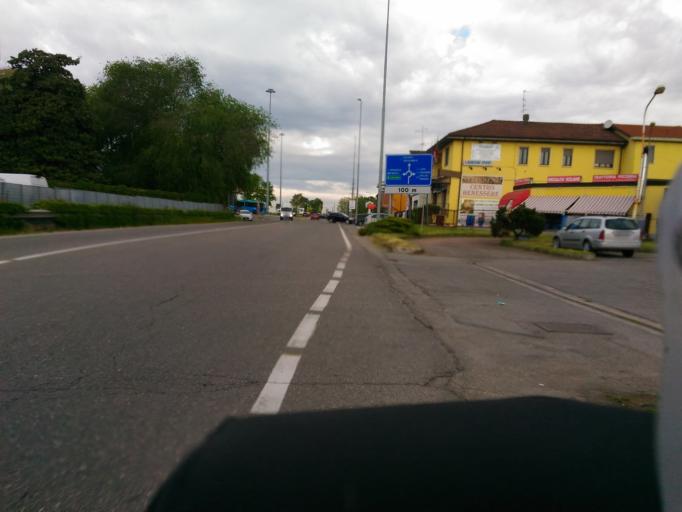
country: IT
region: Lombardy
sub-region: Citta metropolitana di Milano
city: Melegnano
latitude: 45.3641
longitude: 9.3226
